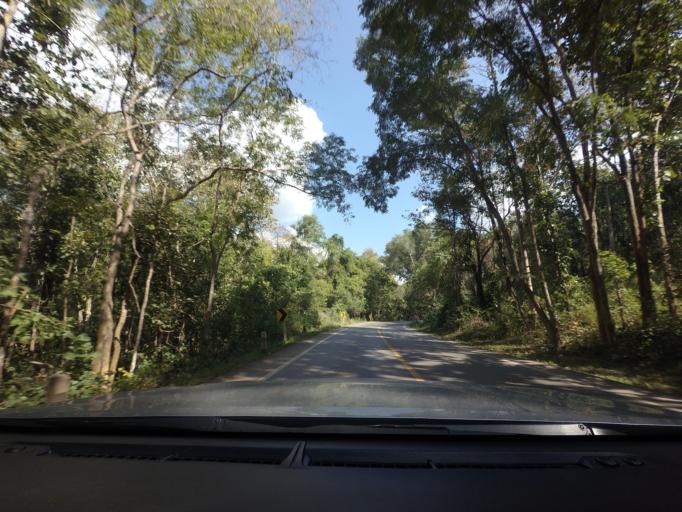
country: TH
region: Chiang Mai
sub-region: Amphoe Chiang Dao
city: Chiang Dao
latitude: 19.4970
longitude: 99.0376
